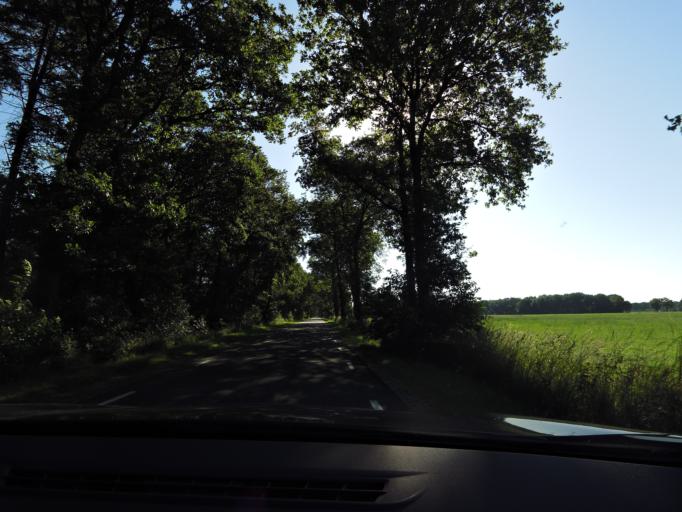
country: NL
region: Overijssel
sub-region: Gemeente Raalte
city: Raalte
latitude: 52.3041
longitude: 6.3113
